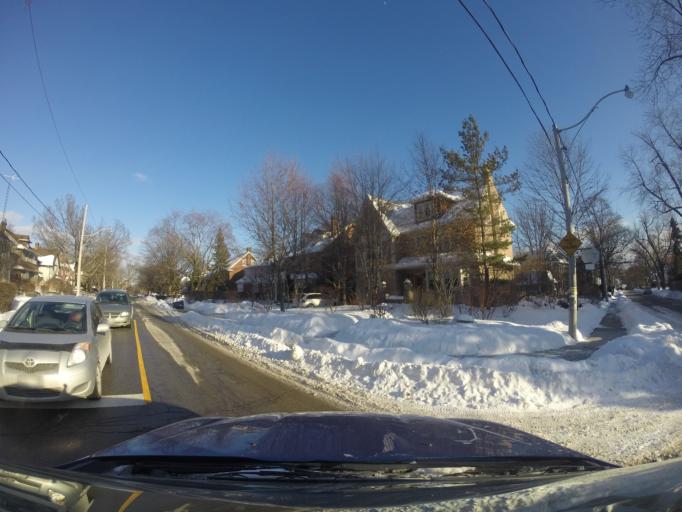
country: CA
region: Ontario
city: Toronto
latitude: 43.7227
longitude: -79.3939
